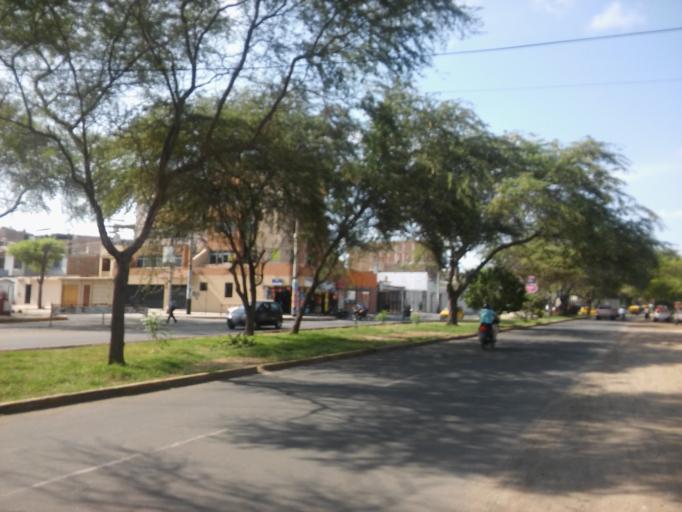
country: PE
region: Piura
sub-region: Provincia de Piura
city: Piura
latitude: -5.1888
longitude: -80.6422
